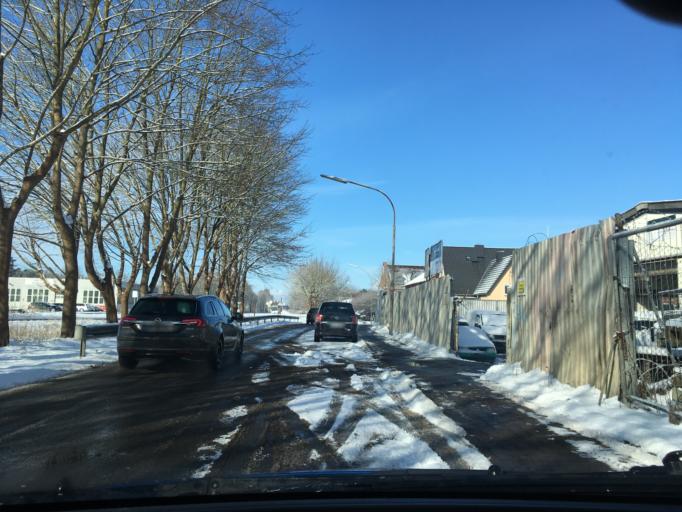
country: DE
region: Lower Saxony
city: Winsen
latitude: 53.3516
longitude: 10.2180
